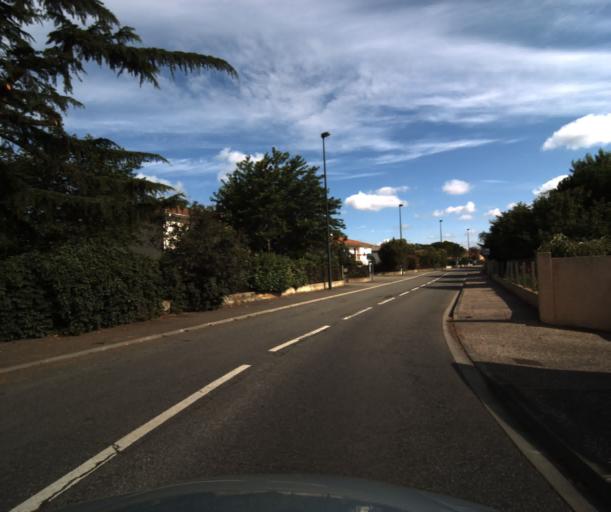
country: FR
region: Midi-Pyrenees
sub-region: Departement de la Haute-Garonne
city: Seysses
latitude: 43.4700
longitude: 1.3186
